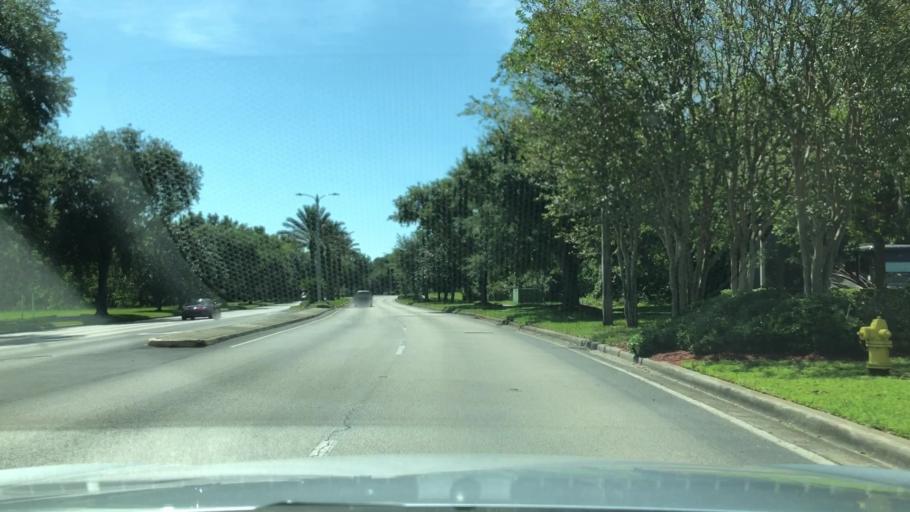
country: US
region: Florida
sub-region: Saint Johns County
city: Saint Augustine
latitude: 29.9231
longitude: -81.4123
